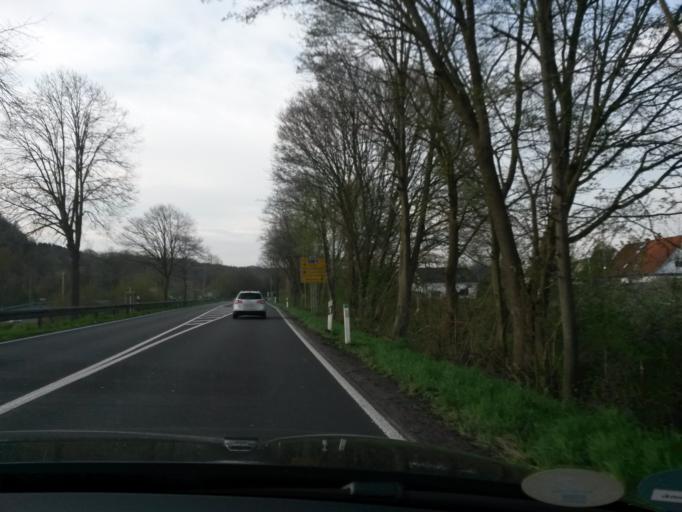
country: DE
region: North Rhine-Westphalia
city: Lohmar
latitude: 50.8834
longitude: 7.2485
